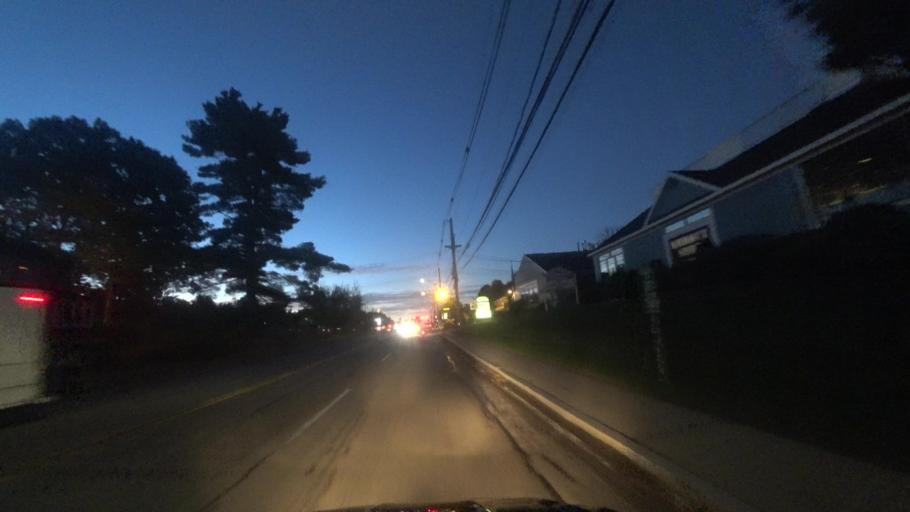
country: US
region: Massachusetts
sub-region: Middlesex County
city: North Reading
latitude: 42.5909
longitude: -71.1174
